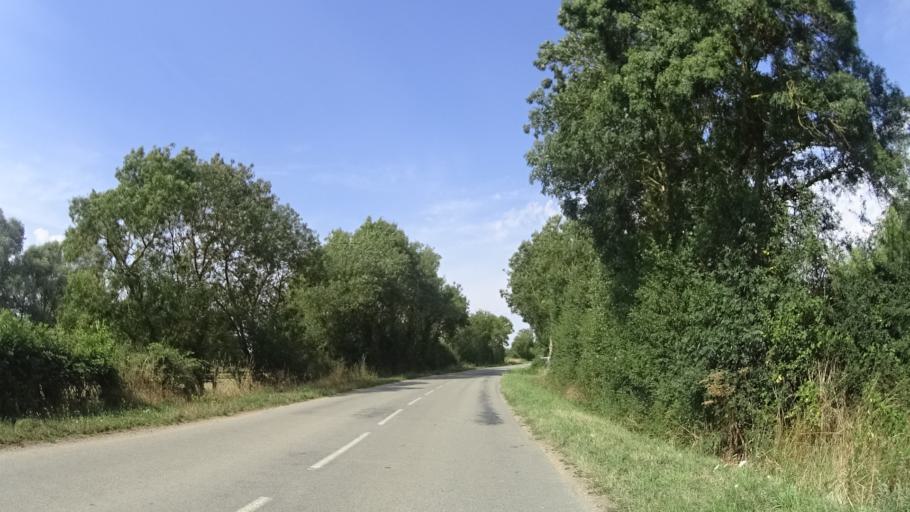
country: FR
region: Pays de la Loire
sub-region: Departement de la Loire-Atlantique
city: Saffre
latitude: 47.4900
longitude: -1.6013
